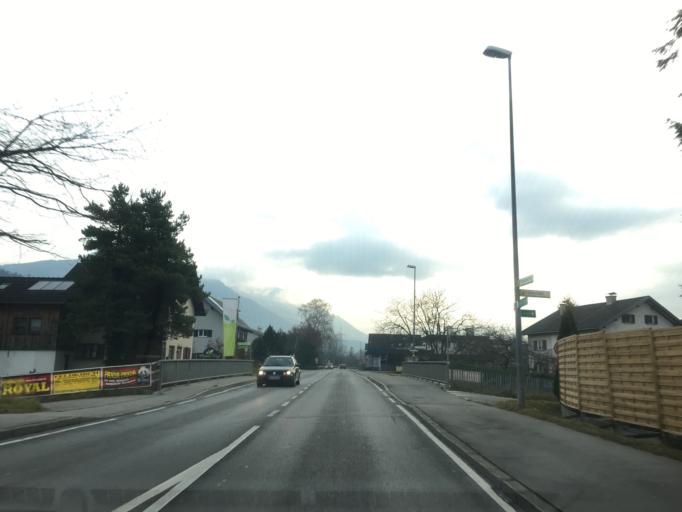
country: AT
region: Vorarlberg
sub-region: Politischer Bezirk Feldkirch
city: Gofis
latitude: 47.2233
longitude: 9.6283
